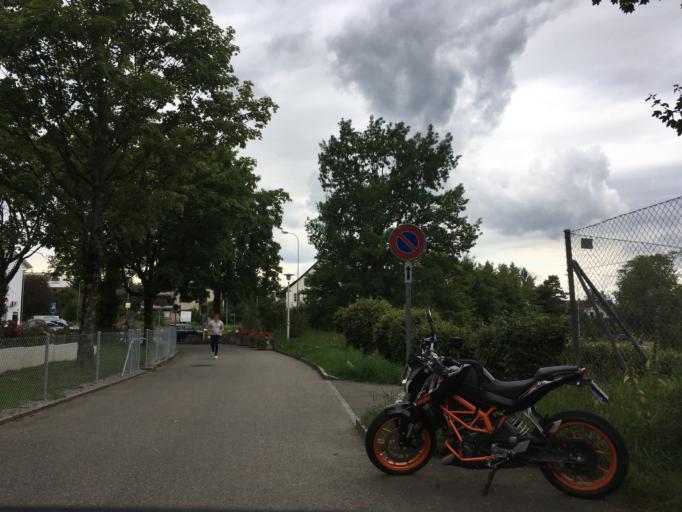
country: CH
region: Zurich
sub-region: Bezirk Uster
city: Dubendorf
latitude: 47.3934
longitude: 8.6234
